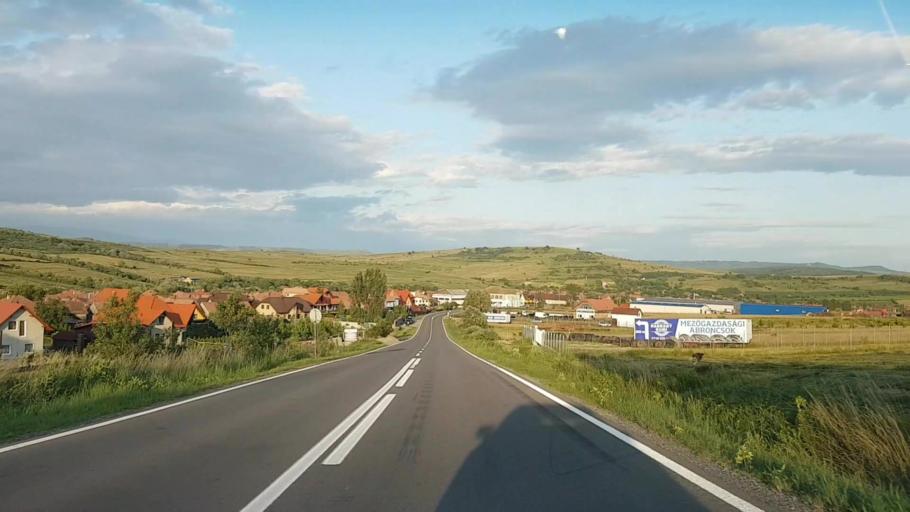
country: RO
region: Harghita
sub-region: Comuna Lupeni
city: Lupeni
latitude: 46.3711
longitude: 25.2249
